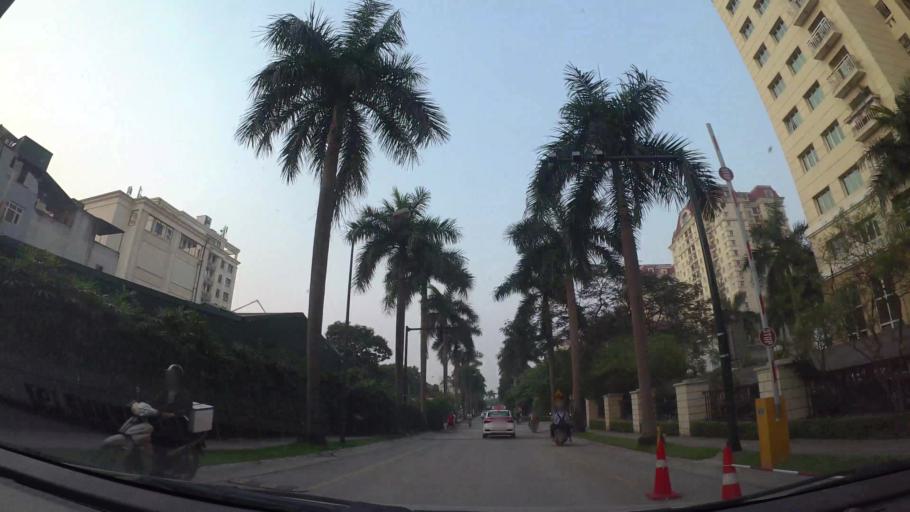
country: VN
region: Ha Noi
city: Tay Ho
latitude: 21.0713
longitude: 105.8078
